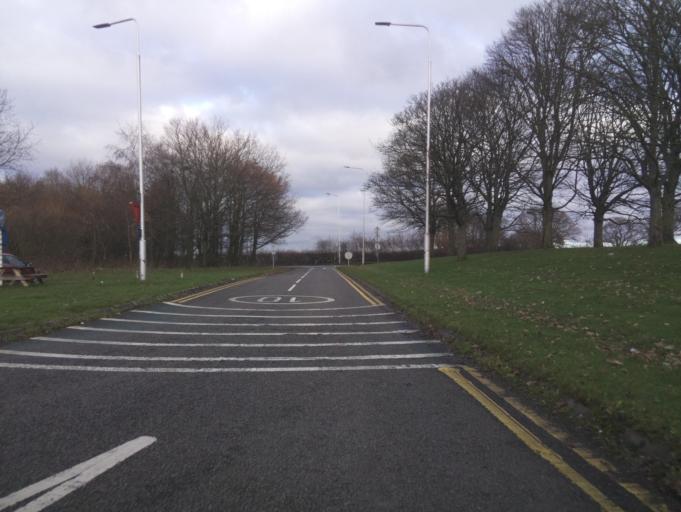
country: GB
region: England
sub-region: Cumbria
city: Scotby
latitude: 54.7984
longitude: -2.8686
